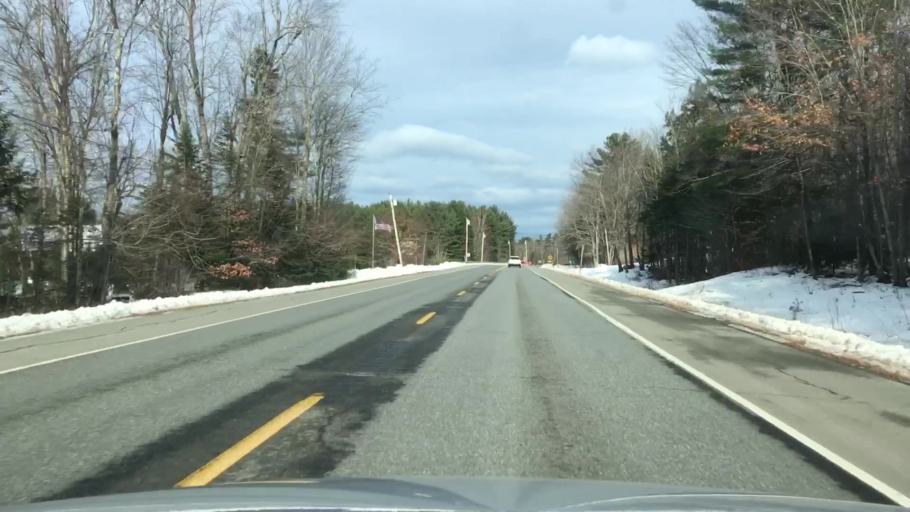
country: US
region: Maine
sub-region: Kennebec County
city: Monmouth
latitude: 44.2514
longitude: -70.0634
